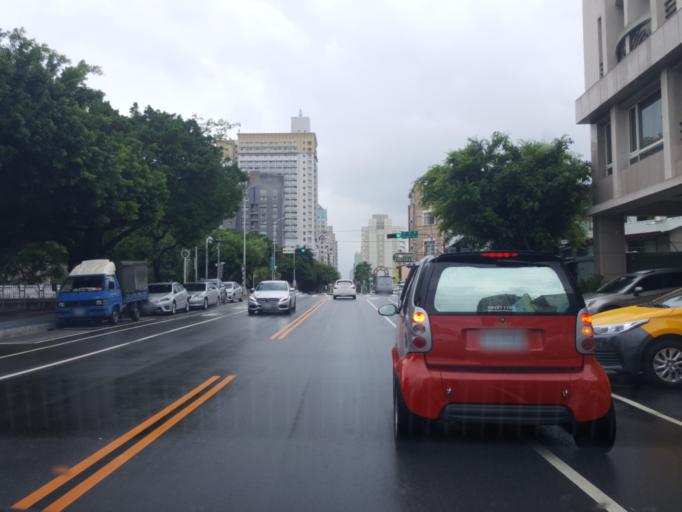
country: TW
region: Taiwan
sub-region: Taichung City
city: Taichung
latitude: 24.1386
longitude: 120.6701
